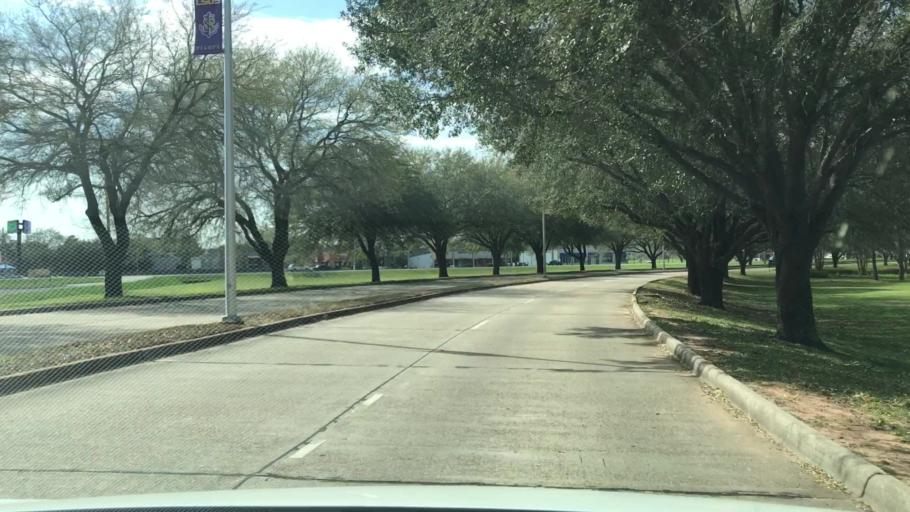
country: US
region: Louisiana
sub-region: Bossier Parish
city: Bossier City
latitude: 32.4254
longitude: -93.7058
